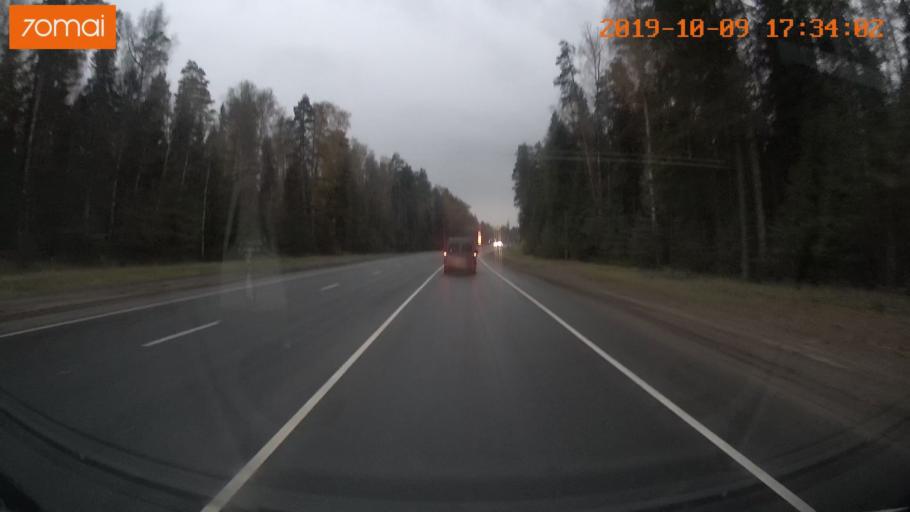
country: RU
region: Ivanovo
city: Bogorodskoye
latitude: 57.1105
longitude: 41.0157
